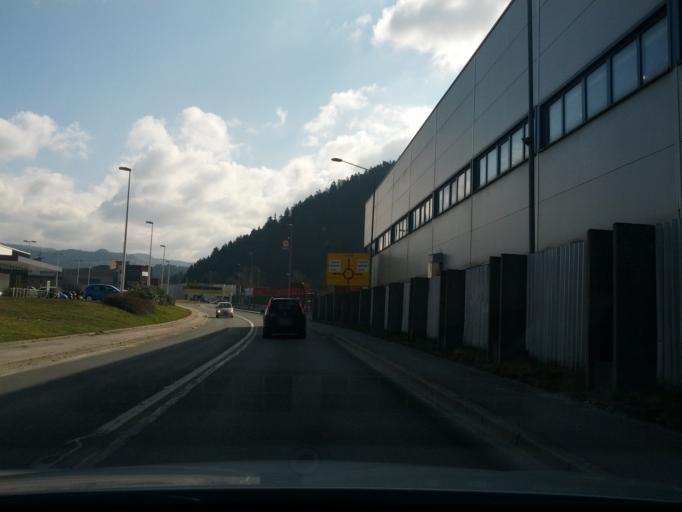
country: SI
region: Litija
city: Litija
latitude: 46.0570
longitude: 14.8188
